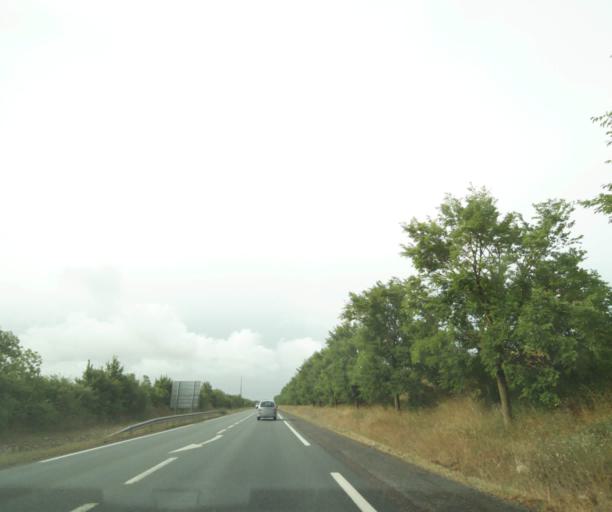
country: FR
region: Poitou-Charentes
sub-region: Departement de la Charente-Maritime
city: Marsilly
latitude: 46.2305
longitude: -1.1241
